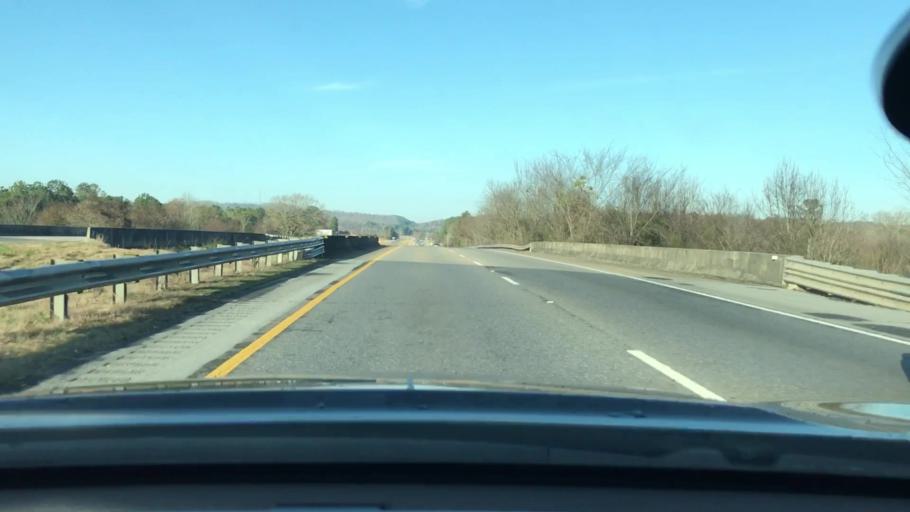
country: US
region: Alabama
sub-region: Shelby County
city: Harpersville
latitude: 33.3468
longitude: -86.4504
